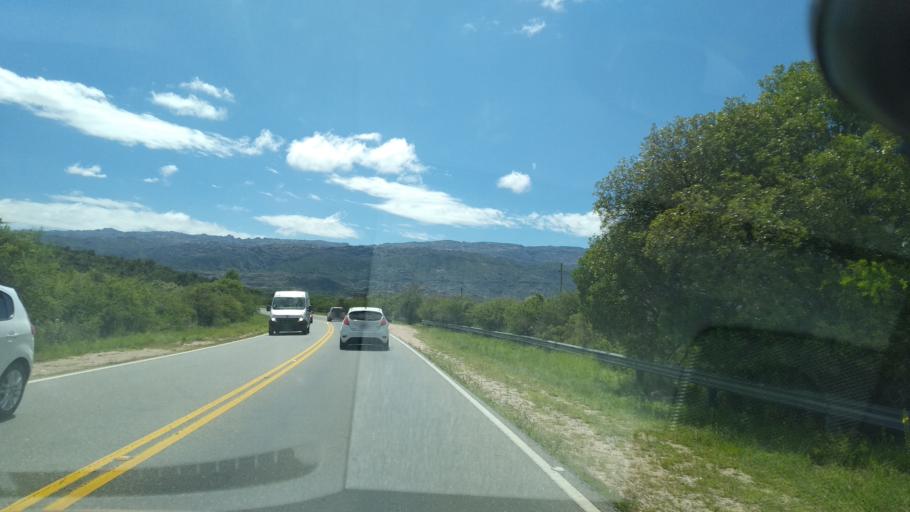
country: AR
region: Cordoba
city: Mina Clavero
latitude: -31.7642
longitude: -64.9669
